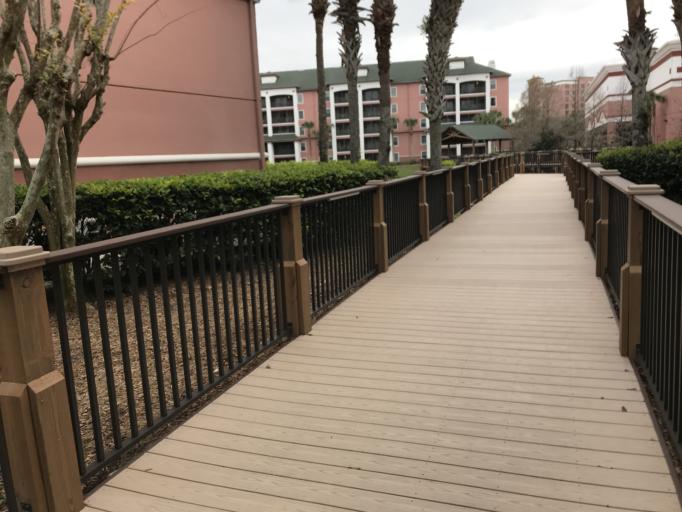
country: US
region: Florida
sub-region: Osceola County
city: Celebration
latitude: 28.3616
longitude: -81.4927
